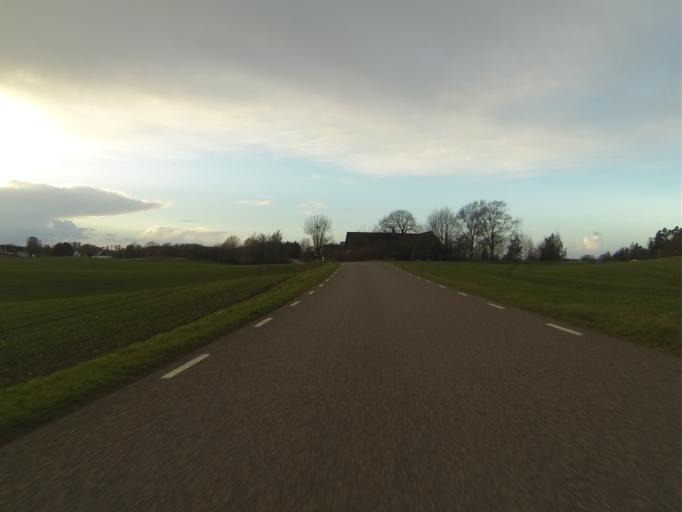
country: SE
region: Skane
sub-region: Lunds Kommun
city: Genarp
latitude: 55.5800
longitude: 13.3497
